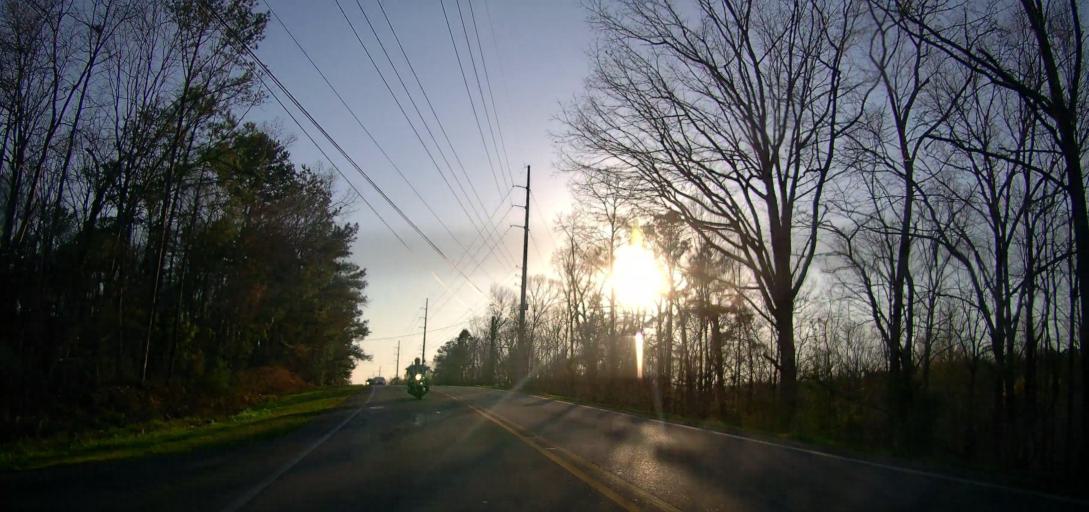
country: US
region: Alabama
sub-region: Shelby County
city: Chelsea
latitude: 33.3485
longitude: -86.6581
